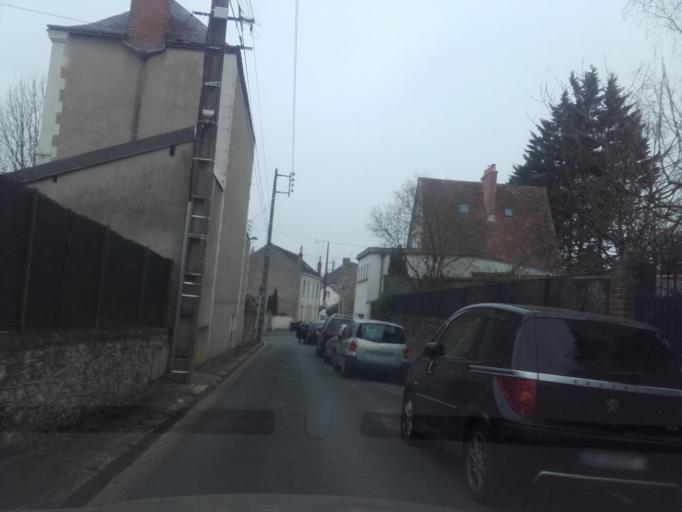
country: FR
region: Centre
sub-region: Departement d'Indre-et-Loire
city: Saint-Cyr-sur-Loire
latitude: 47.4057
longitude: 0.6798
